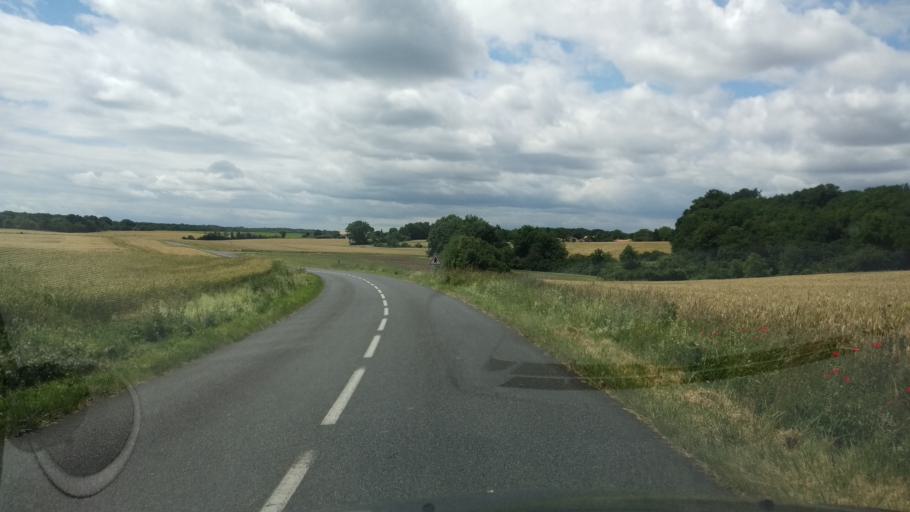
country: FR
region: Poitou-Charentes
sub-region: Departement de la Vienne
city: Vouneuil-sous-Biard
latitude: 46.6033
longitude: 0.2541
